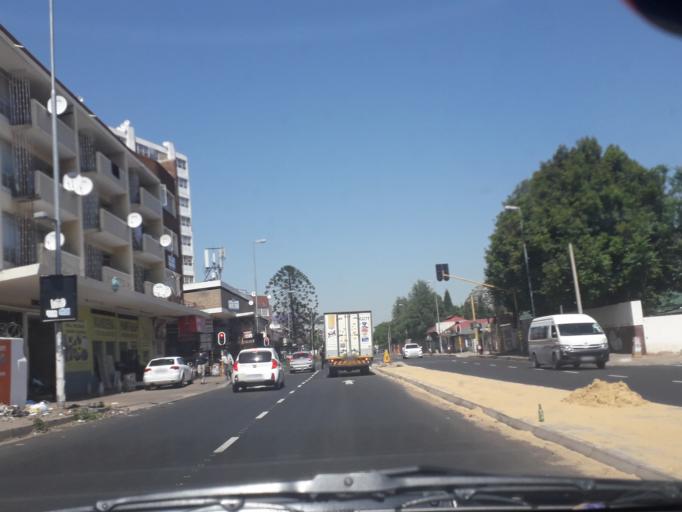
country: ZA
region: Gauteng
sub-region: City of Johannesburg Metropolitan Municipality
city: Johannesburg
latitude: -26.1761
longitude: 28.0653
